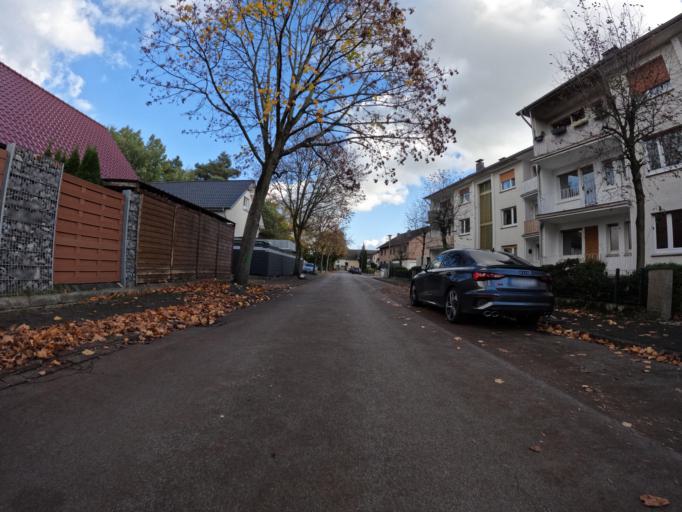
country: DE
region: North Rhine-Westphalia
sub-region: Regierungsbezirk Detmold
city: Hovelhof
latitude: 51.8270
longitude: 8.6414
